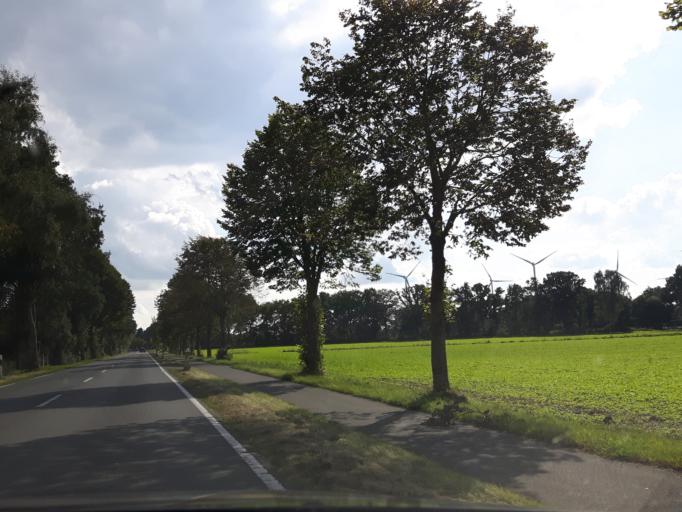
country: DE
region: Lower Saxony
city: Hatten
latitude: 53.0555
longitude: 8.3506
